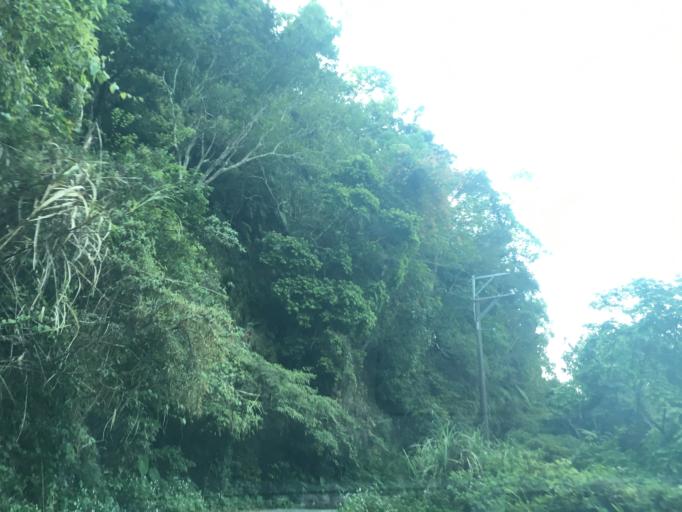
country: TW
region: Taiwan
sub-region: Taichung City
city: Taichung
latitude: 24.1407
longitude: 120.8205
